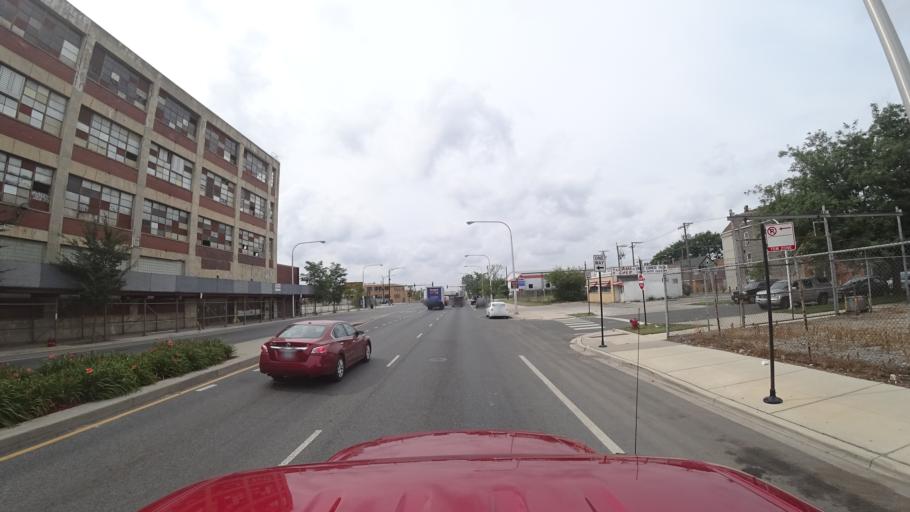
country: US
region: Illinois
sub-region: Cook County
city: Chicago
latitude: 41.8244
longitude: -87.6656
